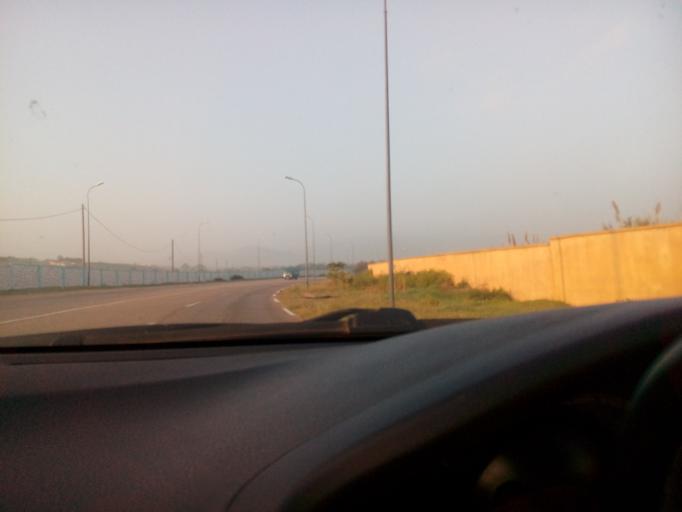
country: DZ
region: Oran
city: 'Ain el Turk
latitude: 35.7128
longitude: -0.8557
